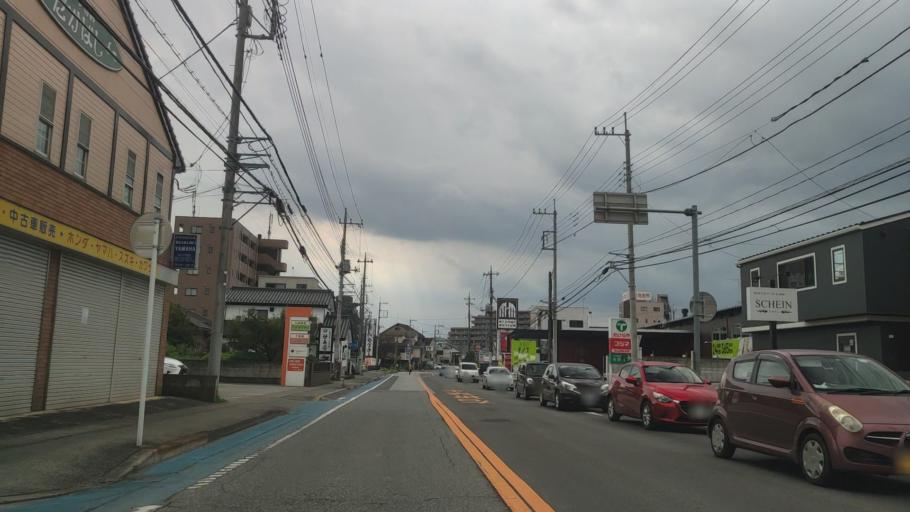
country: JP
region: Tochigi
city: Utsunomiya-shi
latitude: 36.5710
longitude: 139.9156
